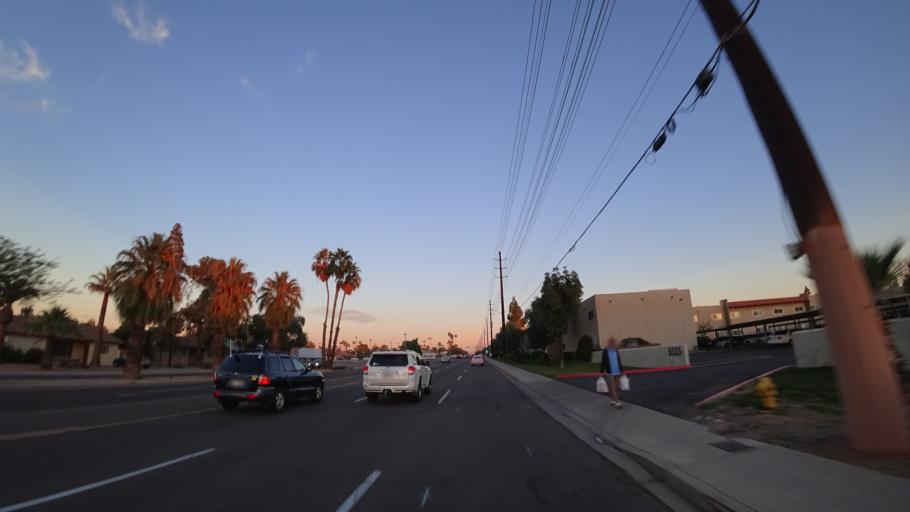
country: US
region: Arizona
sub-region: Maricopa County
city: Paradise Valley
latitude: 33.4799
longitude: -111.9634
